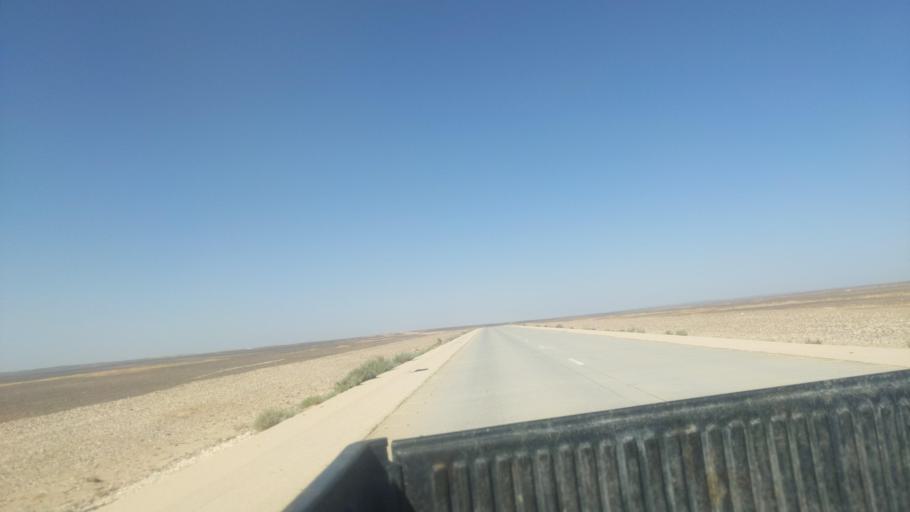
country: JO
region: Amman
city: Al Azraq ash Shamali
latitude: 31.4514
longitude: 36.7735
